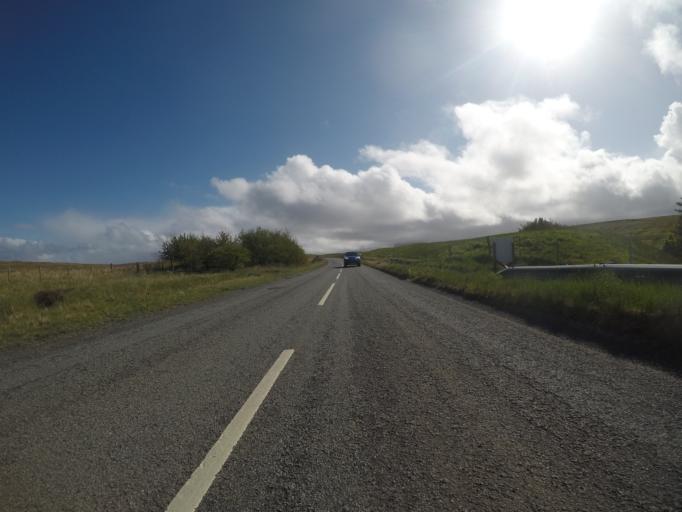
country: GB
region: Scotland
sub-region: Highland
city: Portree
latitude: 57.5804
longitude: -6.1578
